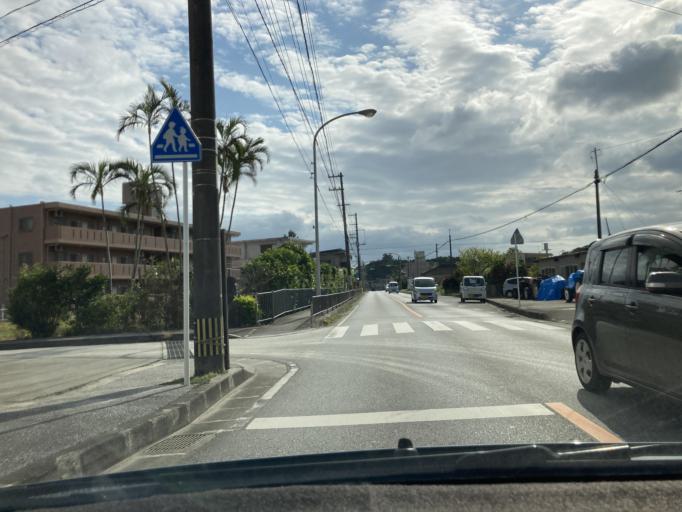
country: JP
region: Okinawa
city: Nago
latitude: 26.6245
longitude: 128.0014
